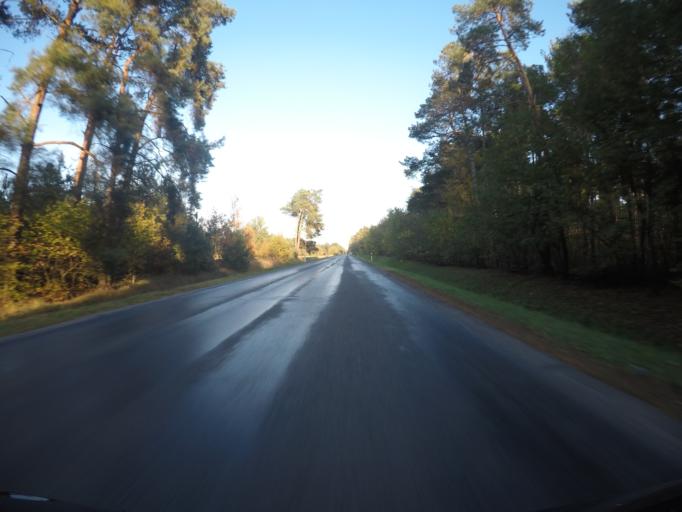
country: HU
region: Somogy
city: Barcs
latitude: 45.9774
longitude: 17.5645
